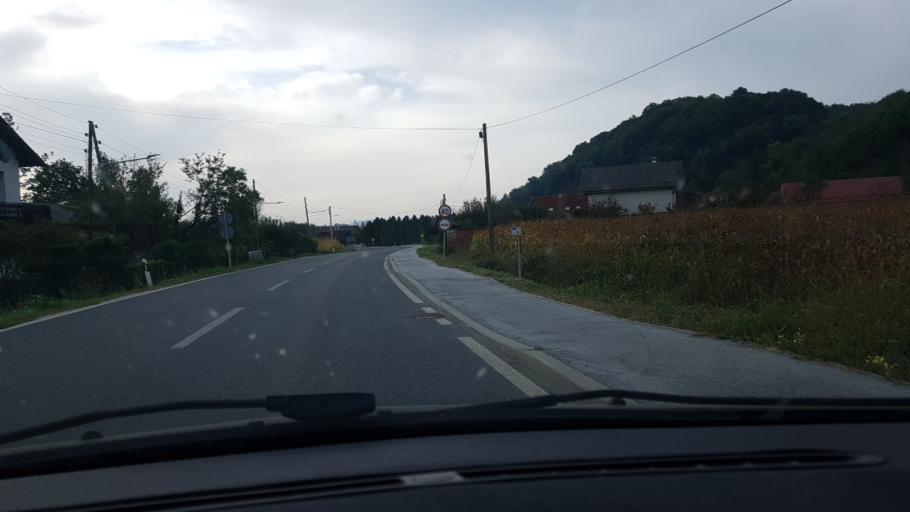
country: HR
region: Krapinsko-Zagorska
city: Zlatar
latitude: 46.1011
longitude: 16.0638
